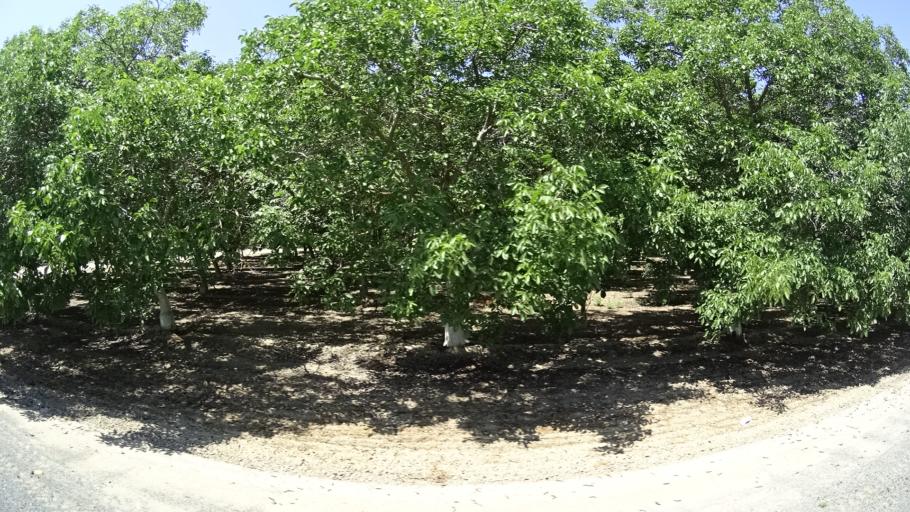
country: US
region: California
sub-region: Kings County
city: Armona
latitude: 36.2875
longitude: -119.7271
